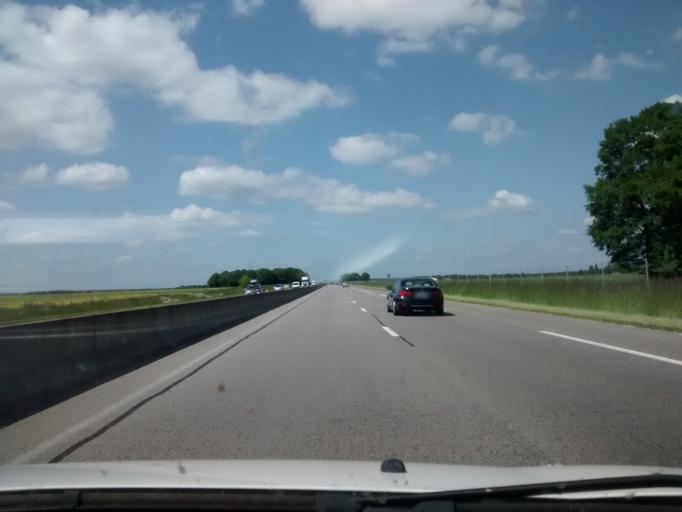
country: FR
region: Ile-de-France
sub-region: Departement des Yvelines
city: Rambouillet
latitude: 48.6030
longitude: 1.8318
